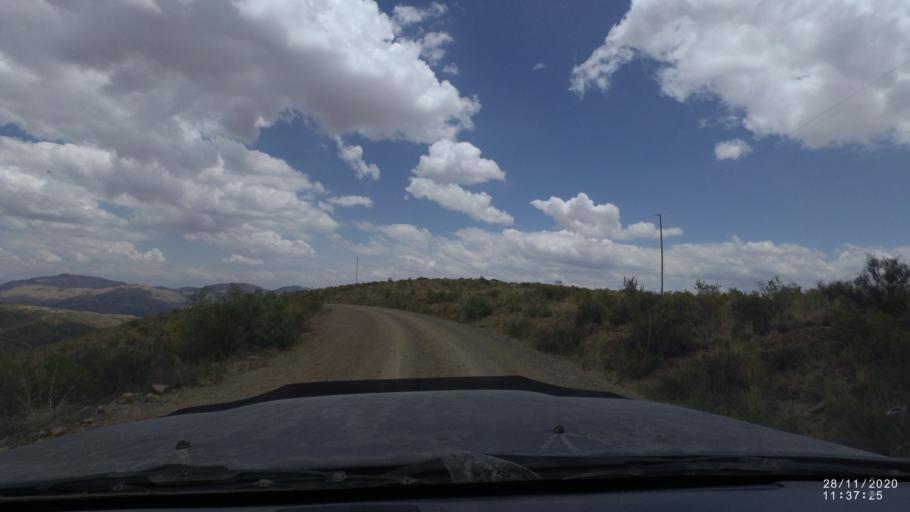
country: BO
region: Cochabamba
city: Tarata
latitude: -17.6772
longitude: -66.0441
